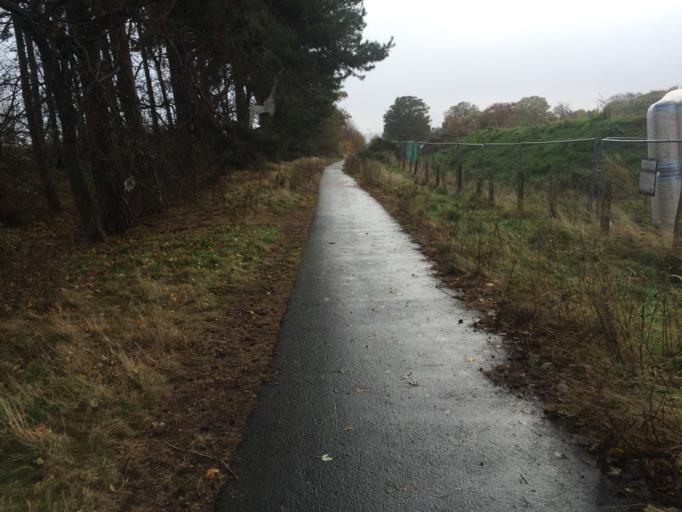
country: GB
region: Scotland
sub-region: Highland
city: Alness
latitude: 57.6925
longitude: -4.2441
